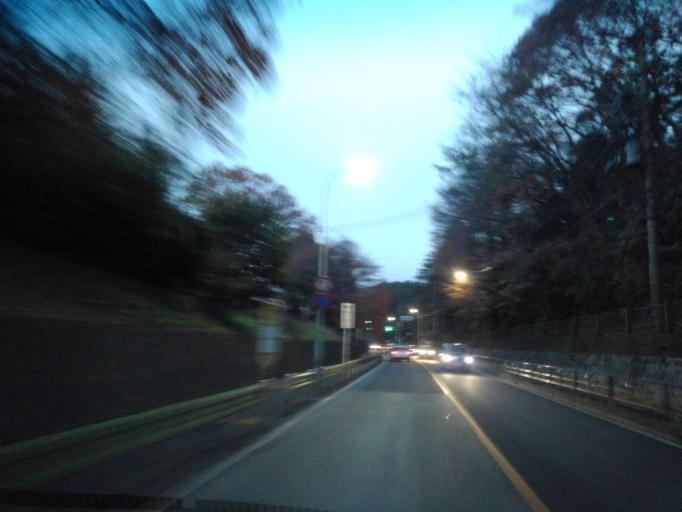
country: JP
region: Tokyo
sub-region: Machida-shi
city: Machida
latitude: 35.5771
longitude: 139.4491
